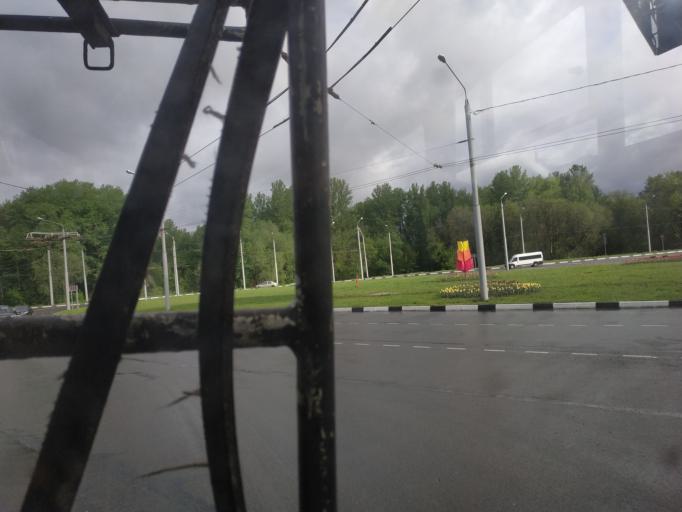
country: RU
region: Brjansk
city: Putevka
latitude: 53.2879
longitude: 34.3039
